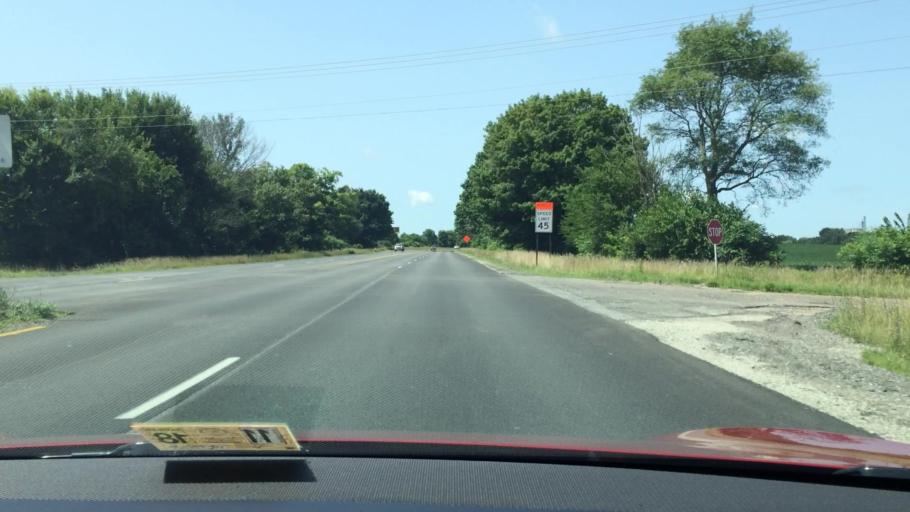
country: US
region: Indiana
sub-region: LaPorte County
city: Hudson Lake
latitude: 41.6716
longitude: -86.6022
